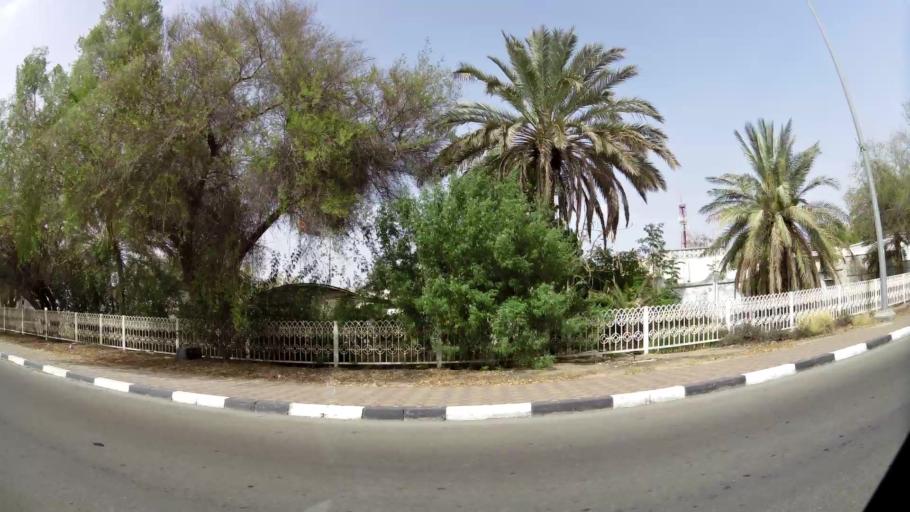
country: AE
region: Abu Dhabi
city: Al Ain
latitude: 24.1884
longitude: 55.6357
